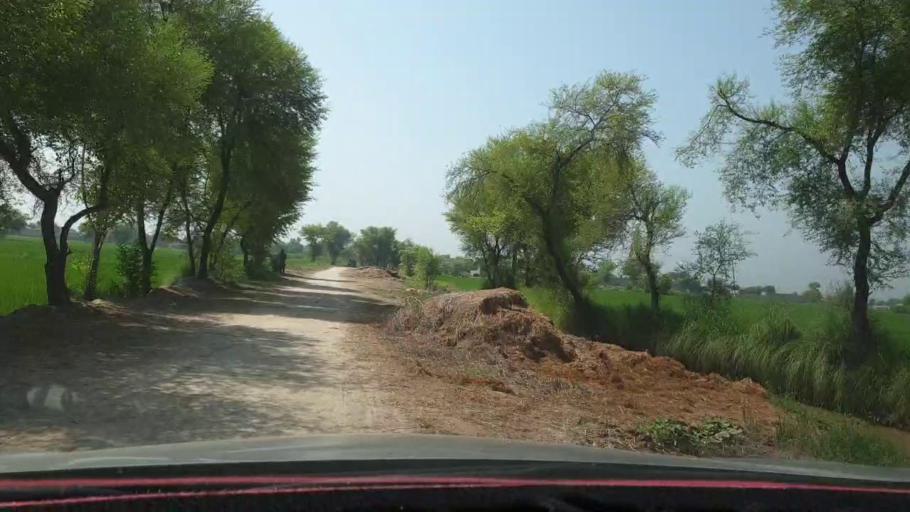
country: PK
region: Sindh
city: Kambar
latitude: 27.5842
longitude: 67.9386
